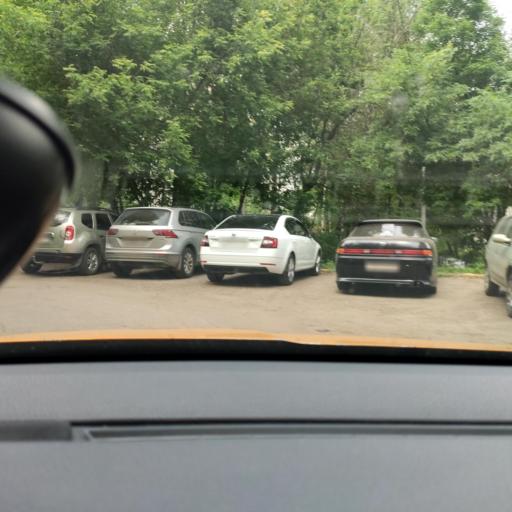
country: RU
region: Moskovskaya
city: Tomilino
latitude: 55.6652
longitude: 37.9591
